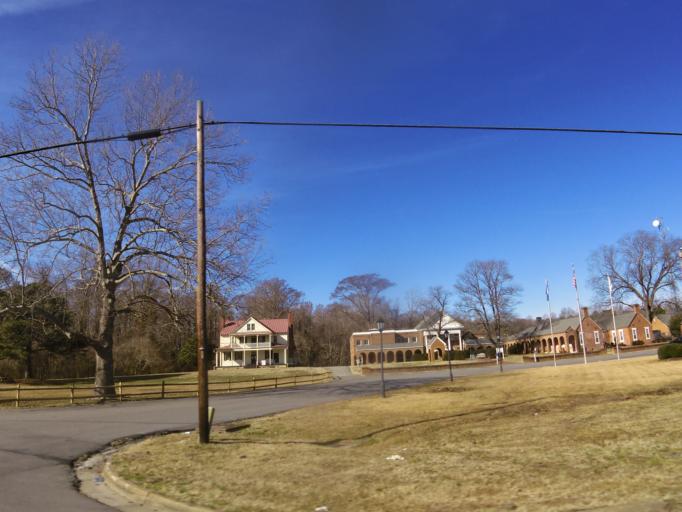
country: US
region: Virginia
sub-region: Isle of Wight County
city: Isle of Wight
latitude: 36.9077
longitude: -76.7081
